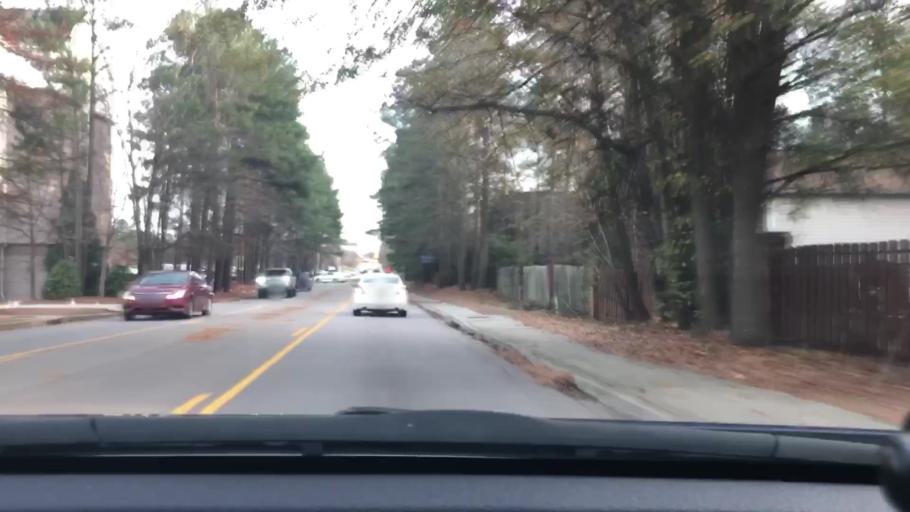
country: US
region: South Carolina
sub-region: Lexington County
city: Irmo
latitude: 34.0874
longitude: -81.1646
